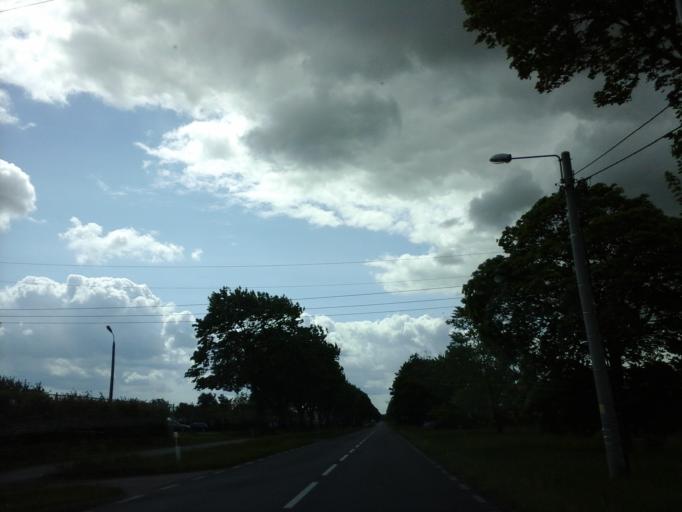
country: PL
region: West Pomeranian Voivodeship
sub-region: Powiat choszczenski
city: Choszczno
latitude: 53.1613
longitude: 15.3973
